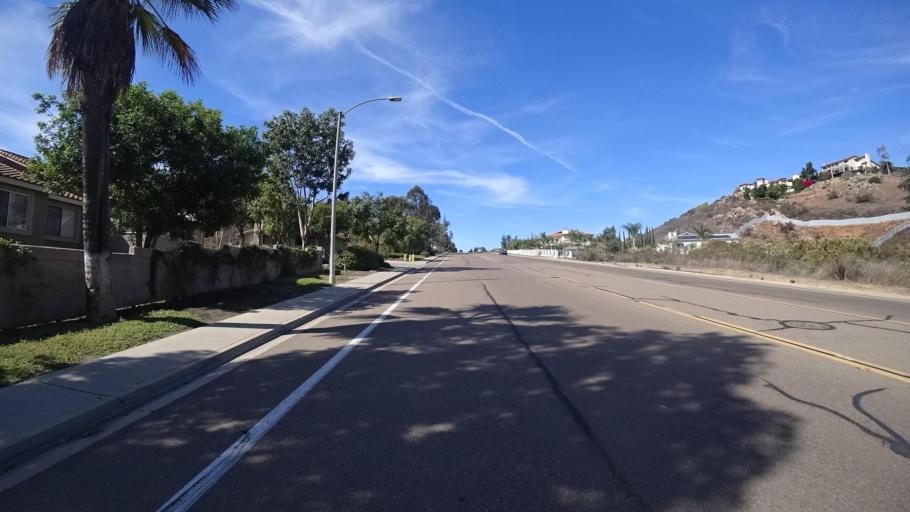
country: US
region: California
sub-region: San Diego County
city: Rancho San Diego
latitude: 32.7513
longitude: -116.9451
